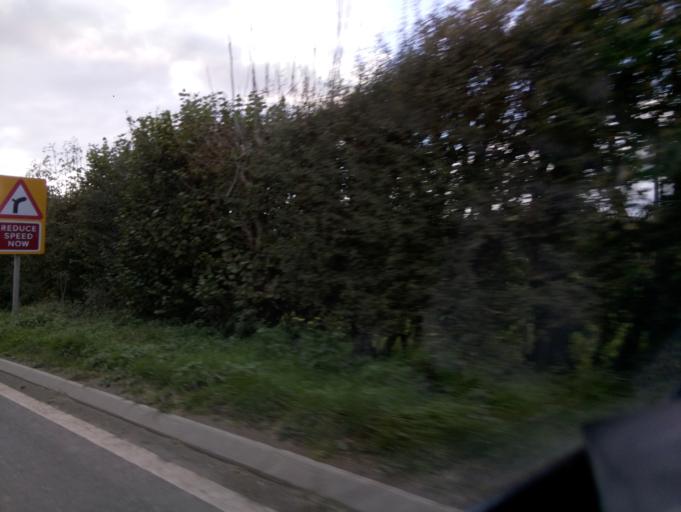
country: GB
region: England
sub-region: Herefordshire
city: Ocle Pychard
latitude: 52.0640
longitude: -2.5859
